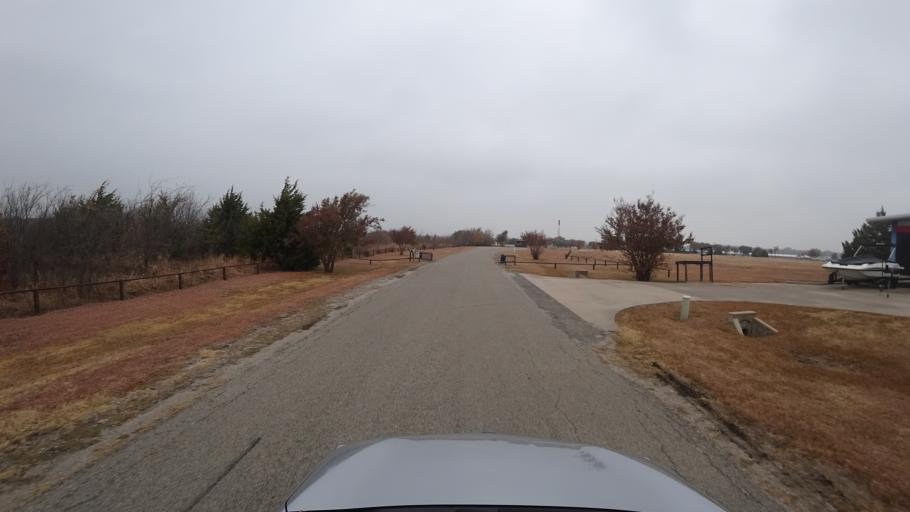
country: US
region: Texas
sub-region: Denton County
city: The Colony
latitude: 33.0724
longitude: -96.9210
